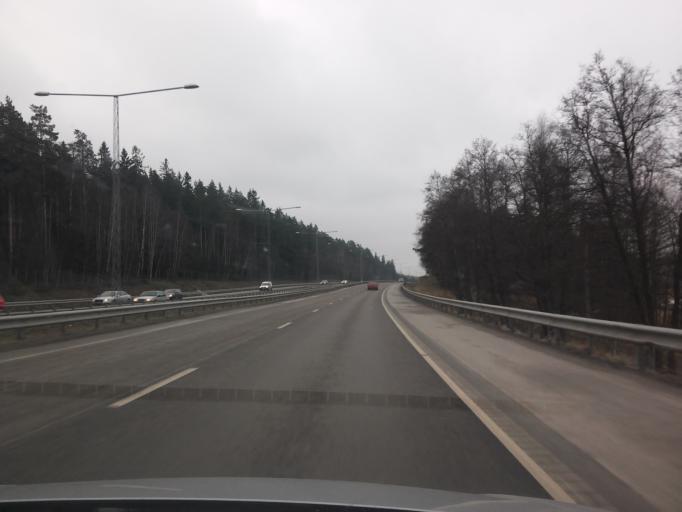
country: SE
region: Stockholm
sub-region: Vallentuna Kommun
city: Vallentuna
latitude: 59.4883
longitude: 18.1652
